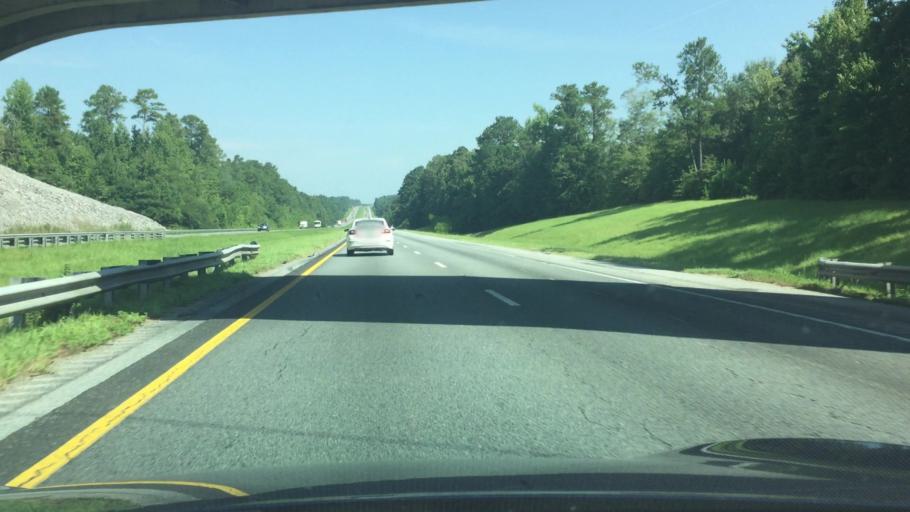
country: US
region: Alabama
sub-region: Autauga County
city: Marbury
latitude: 32.6575
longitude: -86.5000
